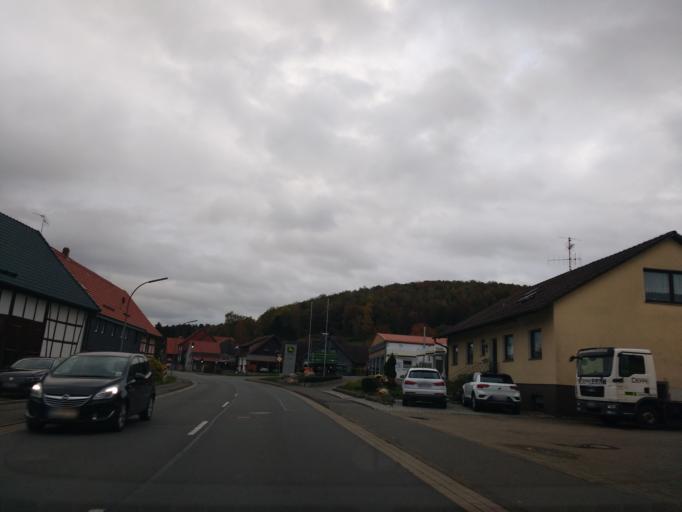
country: DE
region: Lower Saxony
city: Bad Lauterberg im Harz
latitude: 51.6102
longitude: 10.4295
